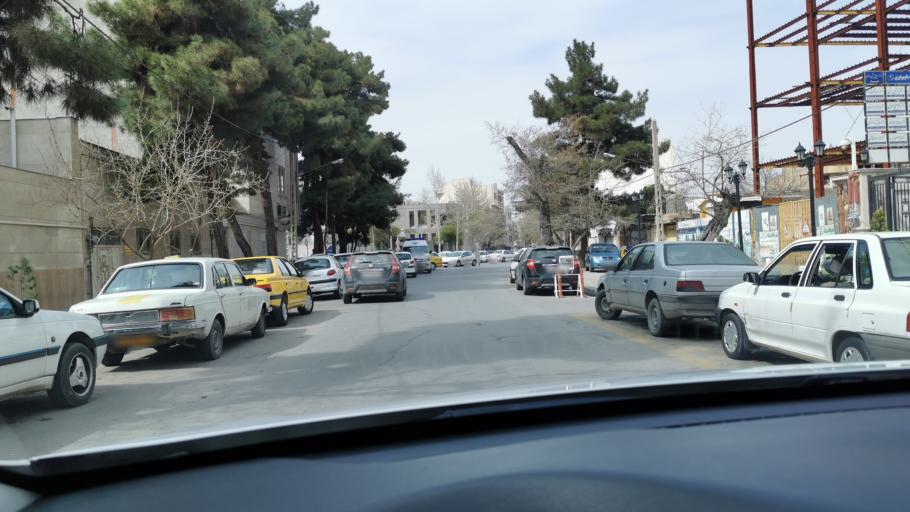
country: IR
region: Razavi Khorasan
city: Mashhad
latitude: 36.2888
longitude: 59.5774
